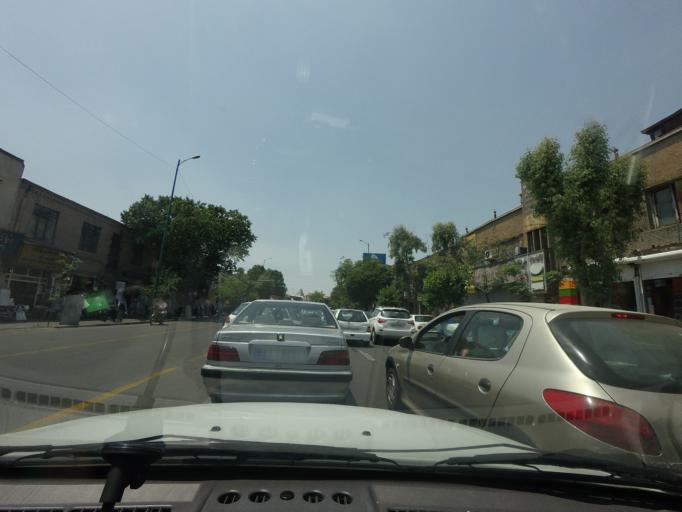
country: IR
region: Tehran
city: Tehran
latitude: 35.6694
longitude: 51.4301
